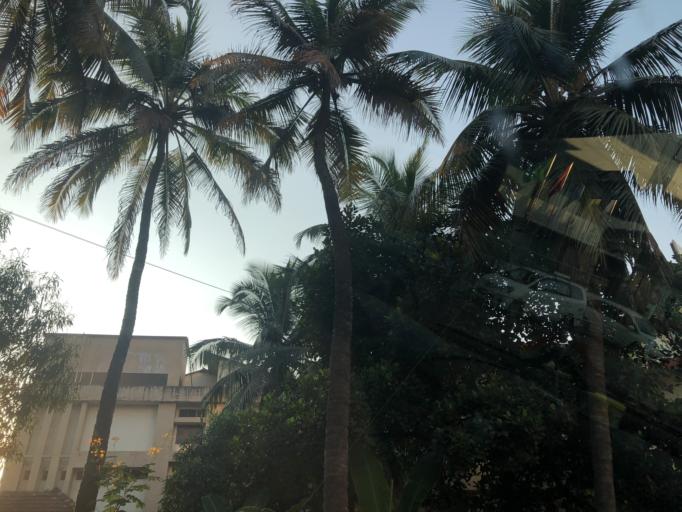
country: IN
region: Karnataka
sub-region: Dakshina Kannada
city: Mangalore
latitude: 12.8771
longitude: 74.8415
